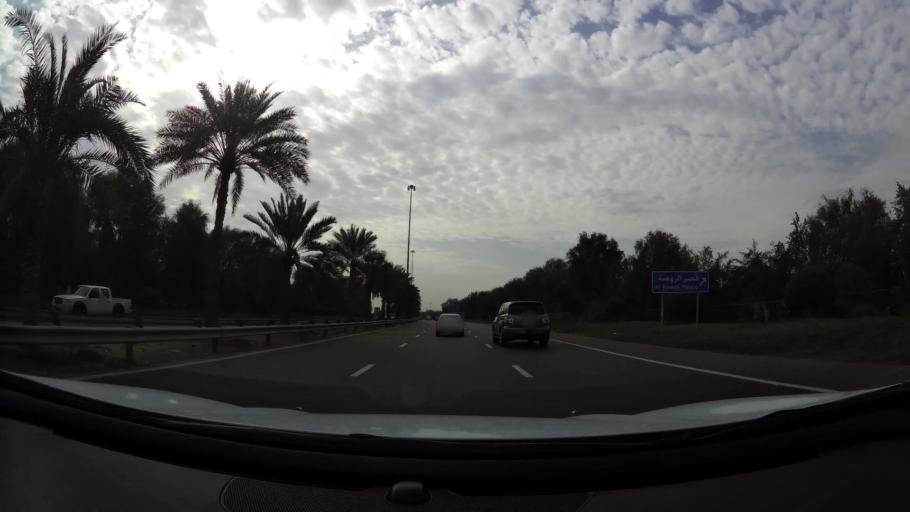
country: AE
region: Abu Dhabi
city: Al Ain
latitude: 24.1910
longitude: 55.5906
